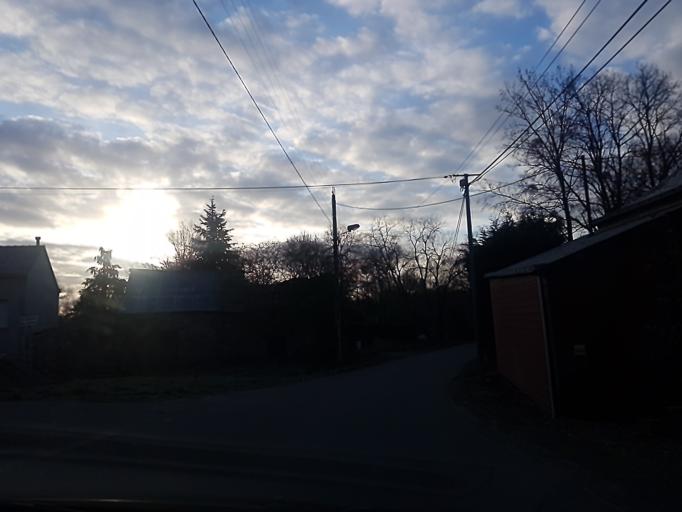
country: FR
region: Pays de la Loire
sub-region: Departement de la Loire-Atlantique
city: Petit-Mars
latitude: 47.3859
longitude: -1.4291
